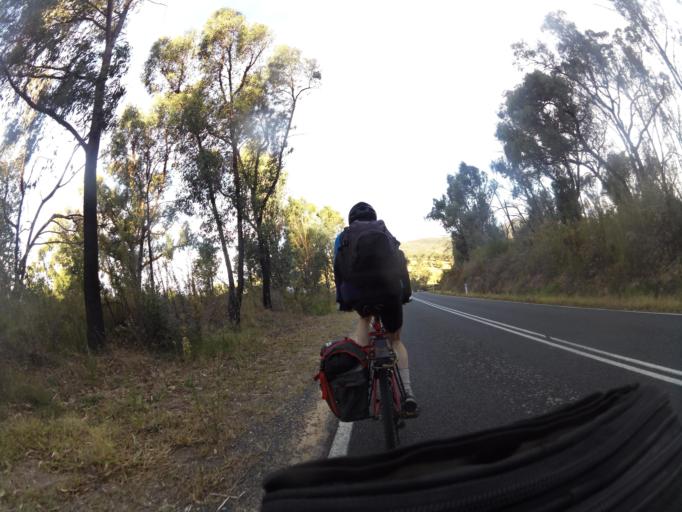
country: AU
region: New South Wales
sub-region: Greater Hume Shire
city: Holbrook
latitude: -35.9995
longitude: 147.8691
